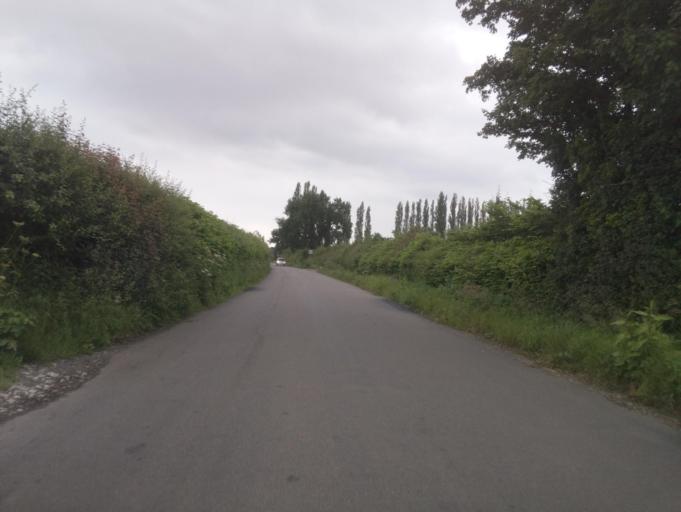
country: GB
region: England
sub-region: Derbyshire
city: Rodsley
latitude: 52.8741
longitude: -1.7143
